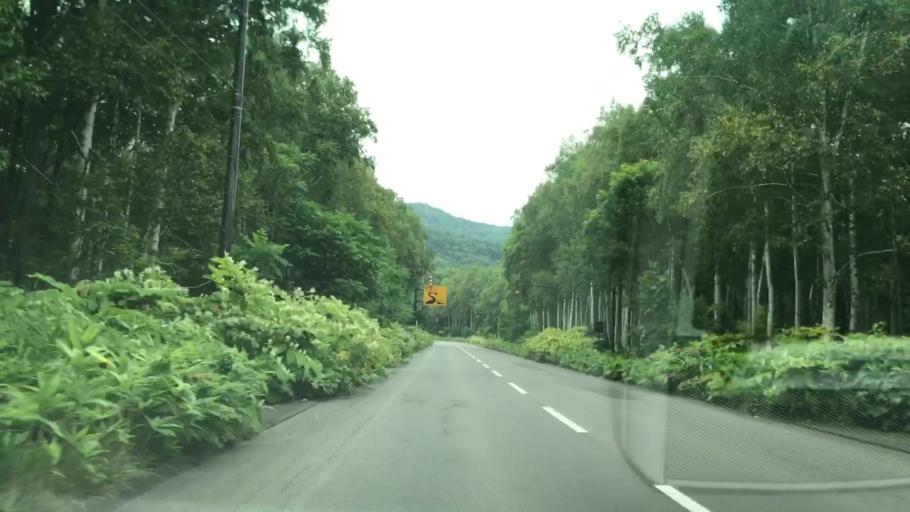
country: JP
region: Hokkaido
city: Yoichi
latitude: 43.0081
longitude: 140.8742
